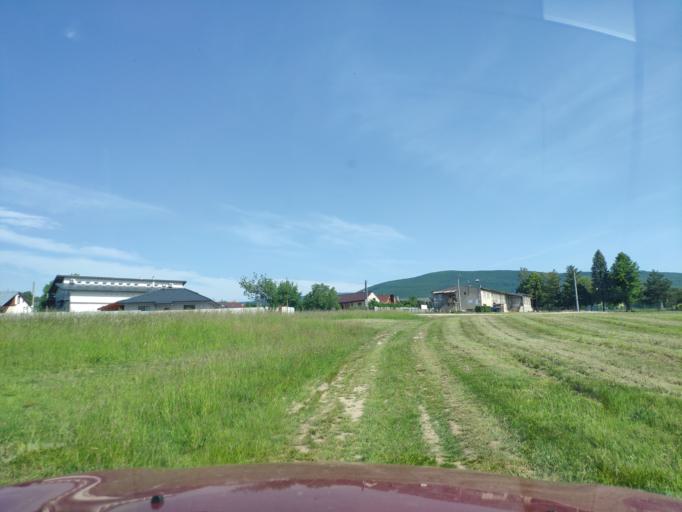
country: SK
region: Kosicky
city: Moldava nad Bodvou
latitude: 48.6920
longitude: 21.0114
